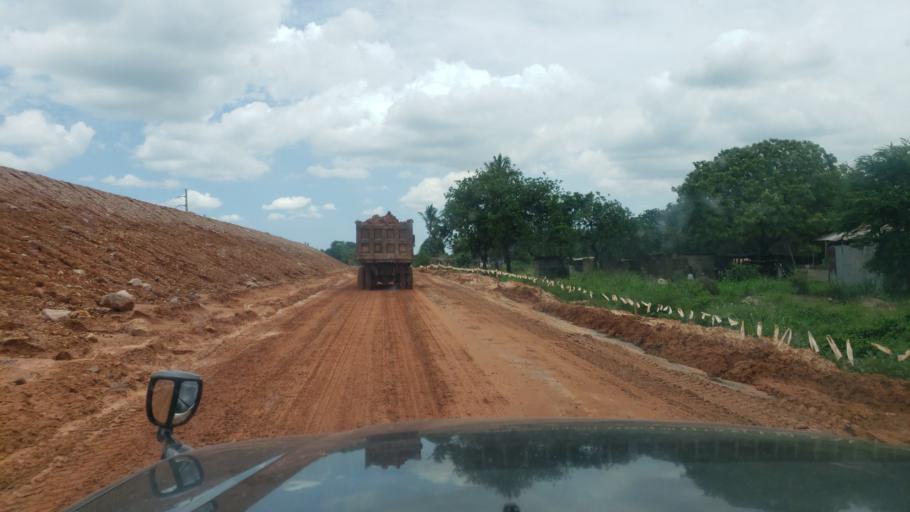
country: TZ
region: Pwani
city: Kisarawe
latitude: -6.8851
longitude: 39.1481
